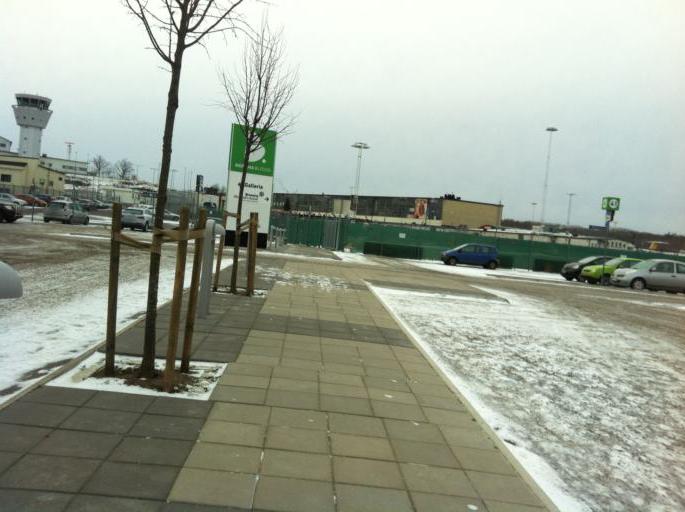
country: SE
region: Stockholm
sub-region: Stockholms Kommun
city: Bromma
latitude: 59.3575
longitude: 17.9476
